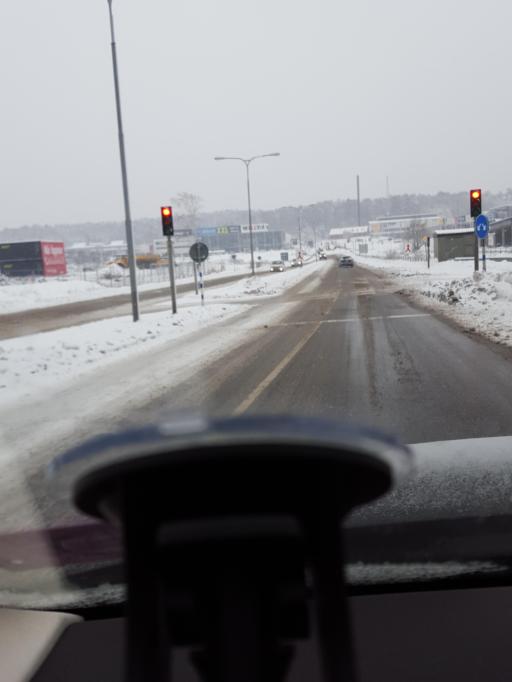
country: SE
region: Vaestra Goetaland
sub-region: Goteborg
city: Majorna
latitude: 57.6439
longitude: 11.9515
